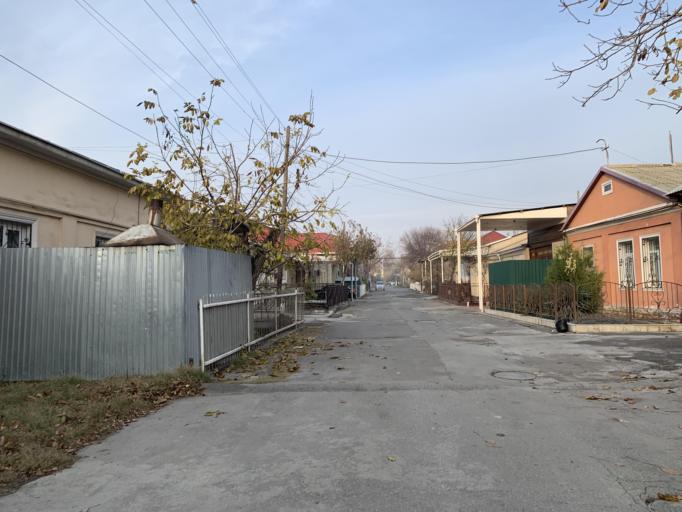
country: UZ
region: Fergana
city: Qo`qon
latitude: 40.5438
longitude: 70.9265
